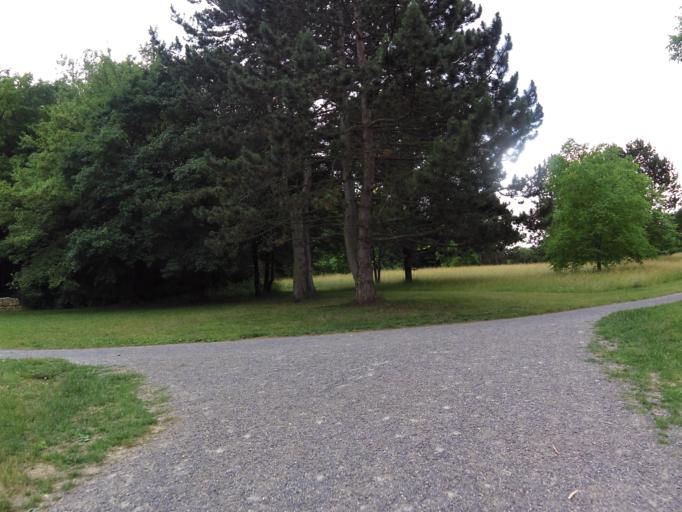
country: DE
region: Bavaria
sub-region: Regierungsbezirk Unterfranken
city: Wuerzburg
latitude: 49.7811
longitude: 9.9570
